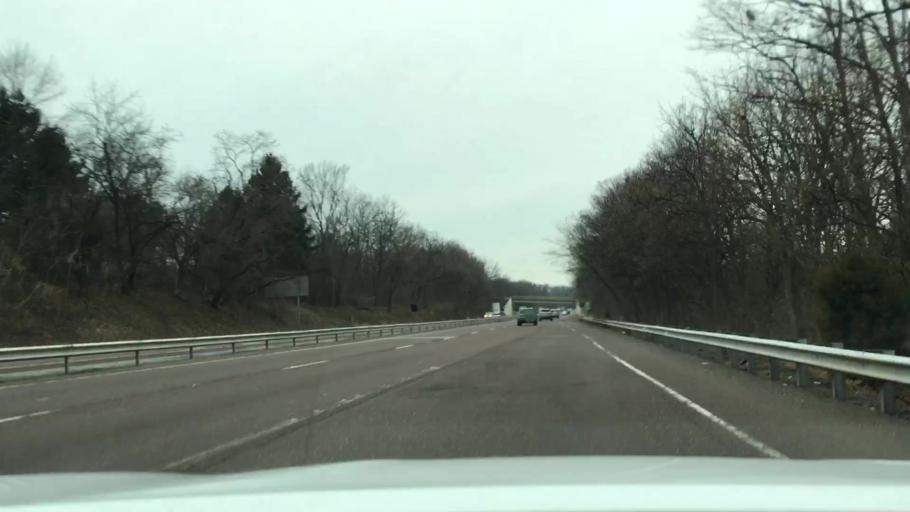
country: US
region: Pennsylvania
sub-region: Chester County
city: Kenilworth
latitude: 40.2319
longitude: -75.6312
